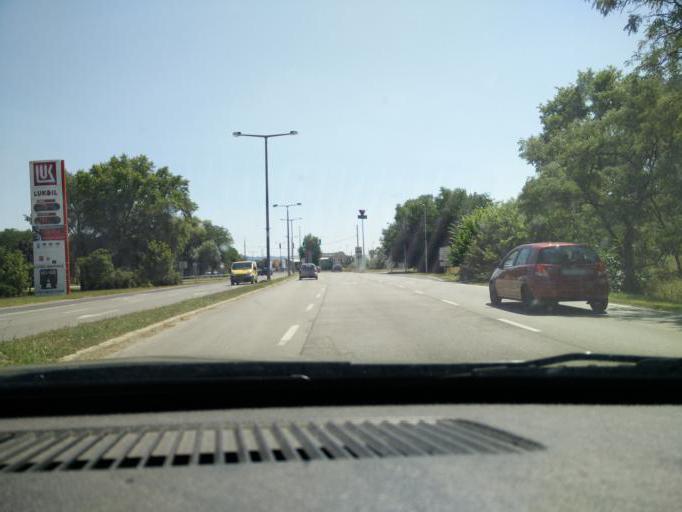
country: HU
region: Komarom-Esztergom
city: Tatabanya
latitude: 47.5982
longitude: 18.3871
